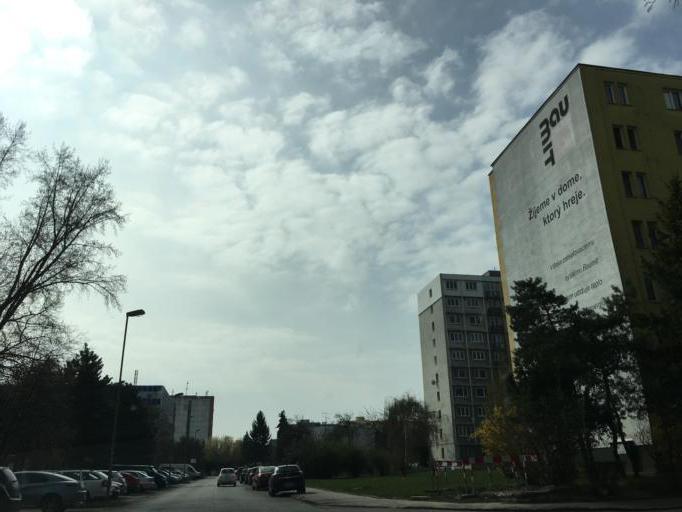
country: SK
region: Bratislavsky
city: Bratislava
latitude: 48.1546
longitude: 17.1621
